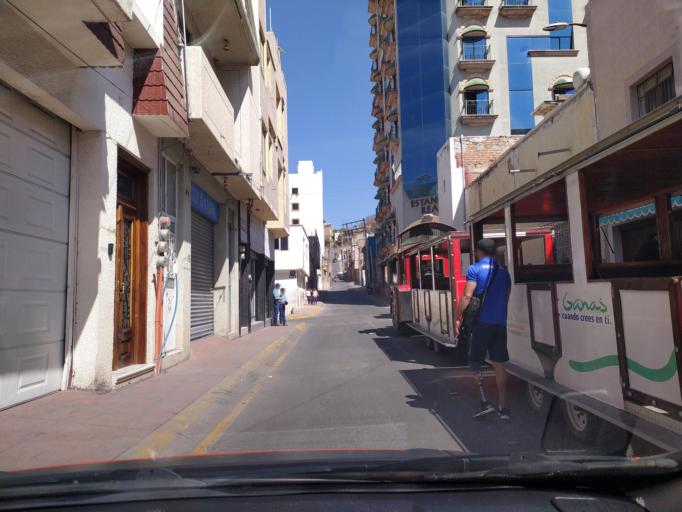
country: MX
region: Jalisco
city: San Juan de los Lagos
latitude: 21.2481
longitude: -102.3319
